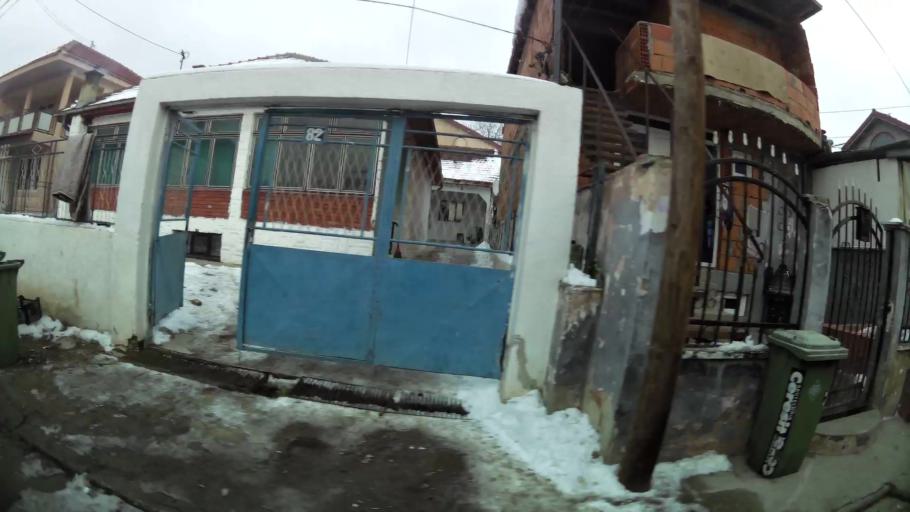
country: MK
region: Suto Orizari
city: Suto Orizare
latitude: 42.0423
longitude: 21.4245
